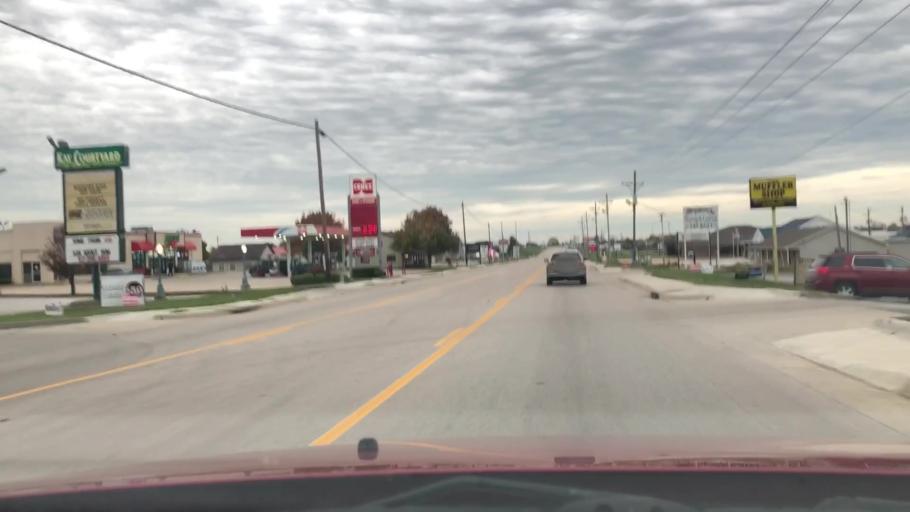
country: US
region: Missouri
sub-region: Dallas County
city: Buffalo
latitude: 37.6331
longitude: -93.1045
